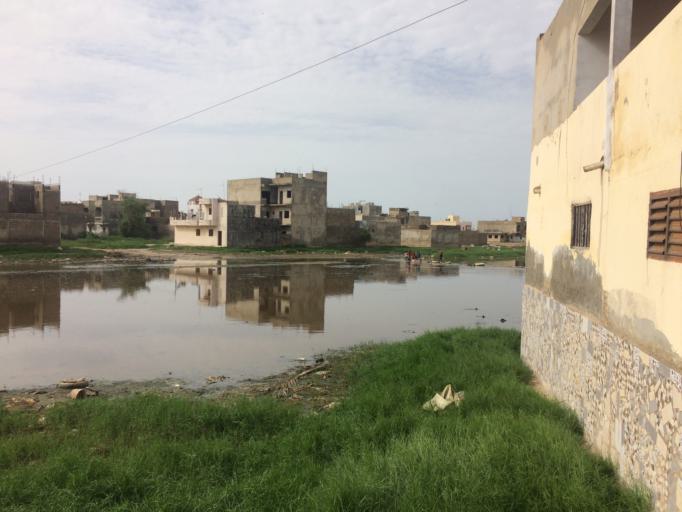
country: SN
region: Dakar
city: Pikine
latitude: 14.7375
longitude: -17.3257
